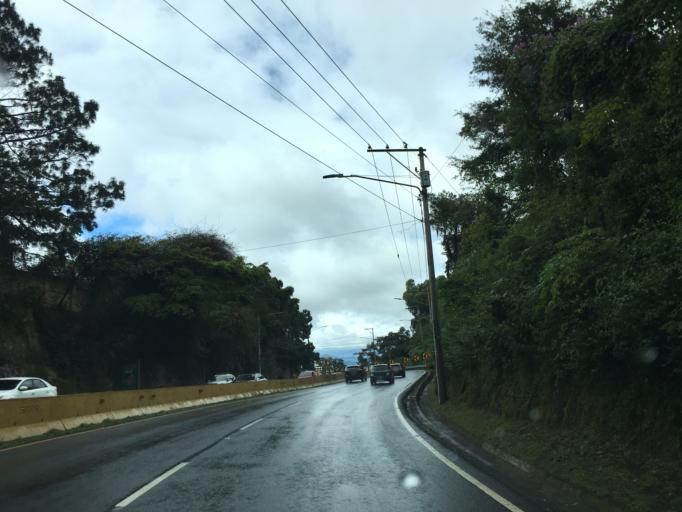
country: GT
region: Guatemala
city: Santa Catarina Pinula
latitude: 14.5780
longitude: -90.4863
